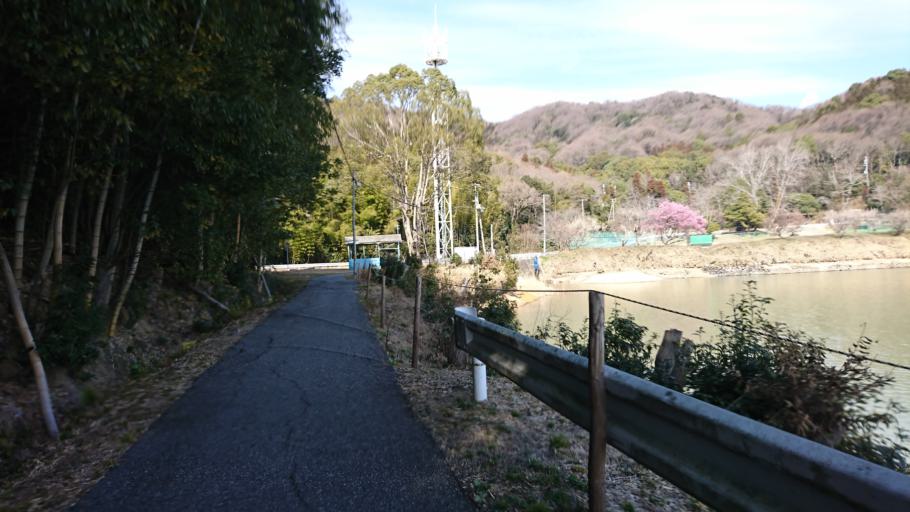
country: JP
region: Hyogo
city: Kakogawacho-honmachi
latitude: 34.8280
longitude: 134.8091
